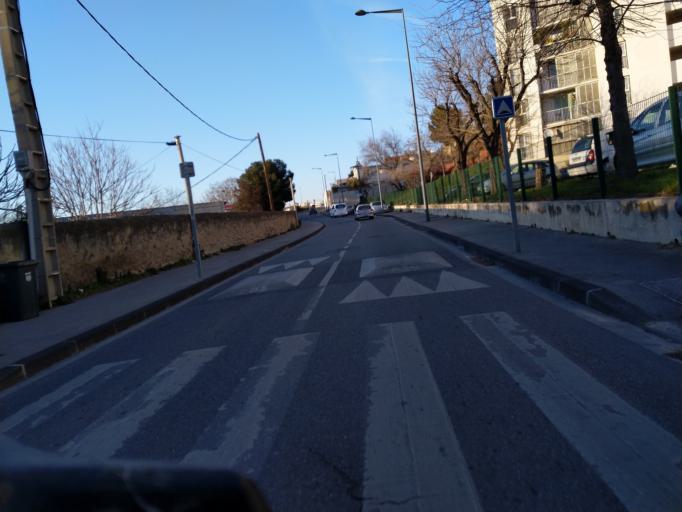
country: FR
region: Provence-Alpes-Cote d'Azur
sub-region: Departement des Bouches-du-Rhone
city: Marseille 12
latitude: 43.2915
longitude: 5.4259
